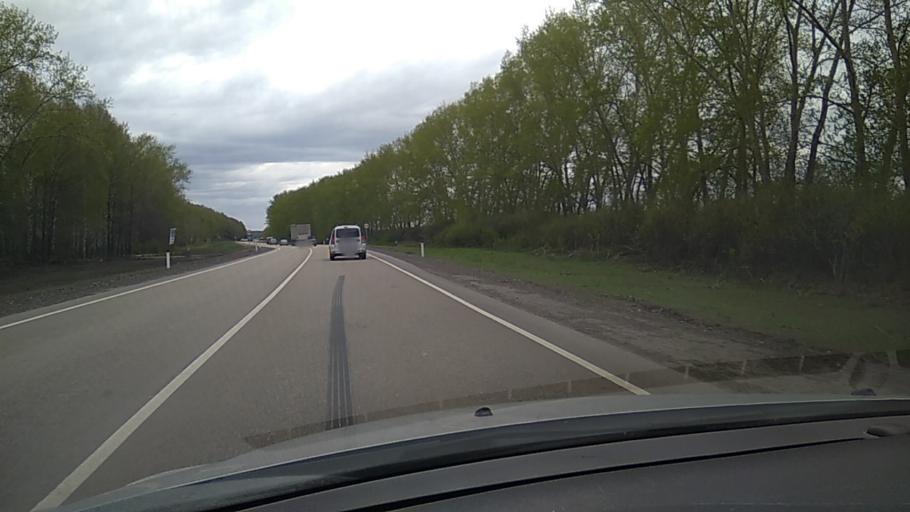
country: RU
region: Sverdlovsk
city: Dvurechensk
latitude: 56.6474
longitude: 61.2081
